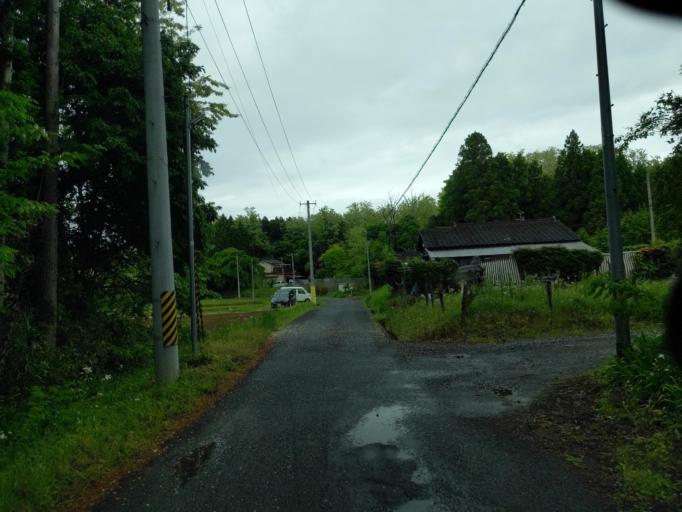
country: JP
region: Fukushima
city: Koriyama
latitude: 37.3420
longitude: 140.3917
